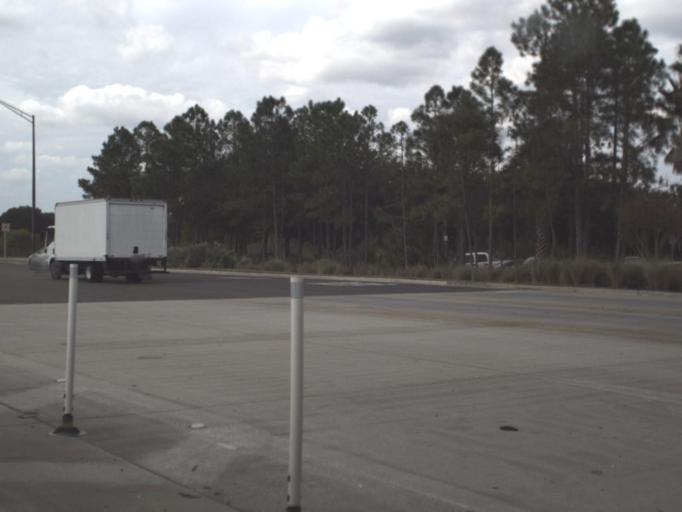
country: US
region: Florida
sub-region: Polk County
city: Lakeland Highlands
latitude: 27.9959
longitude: -81.9348
